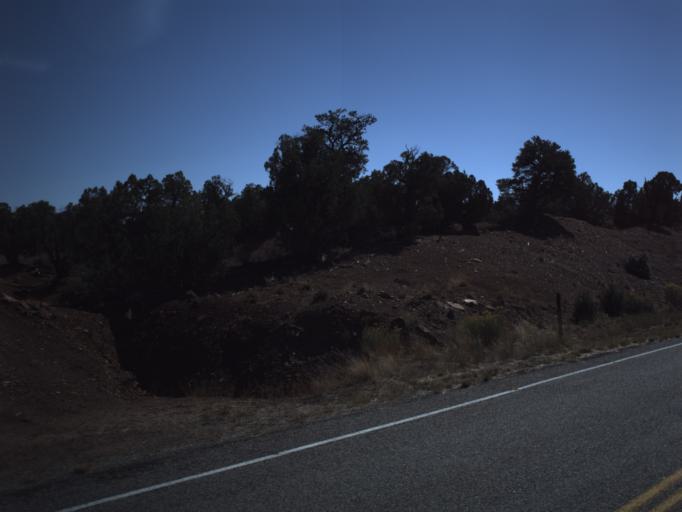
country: US
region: Utah
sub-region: San Juan County
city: Blanding
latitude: 37.5732
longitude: -110.0376
